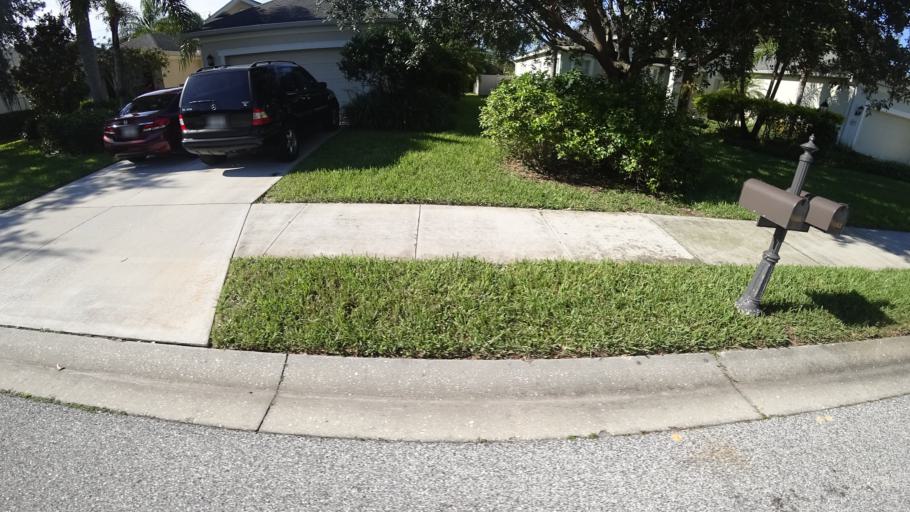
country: US
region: Florida
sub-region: Manatee County
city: West Bradenton
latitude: 27.5151
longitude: -82.6512
